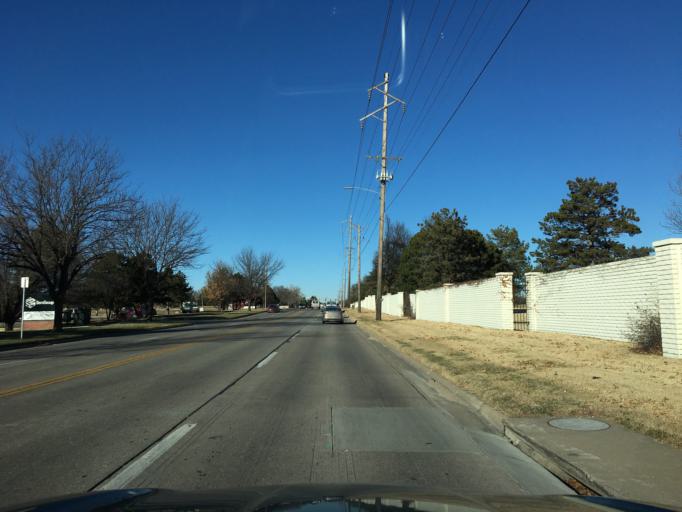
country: US
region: Kansas
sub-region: Sedgwick County
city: Bellaire
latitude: 37.7049
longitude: -97.2446
